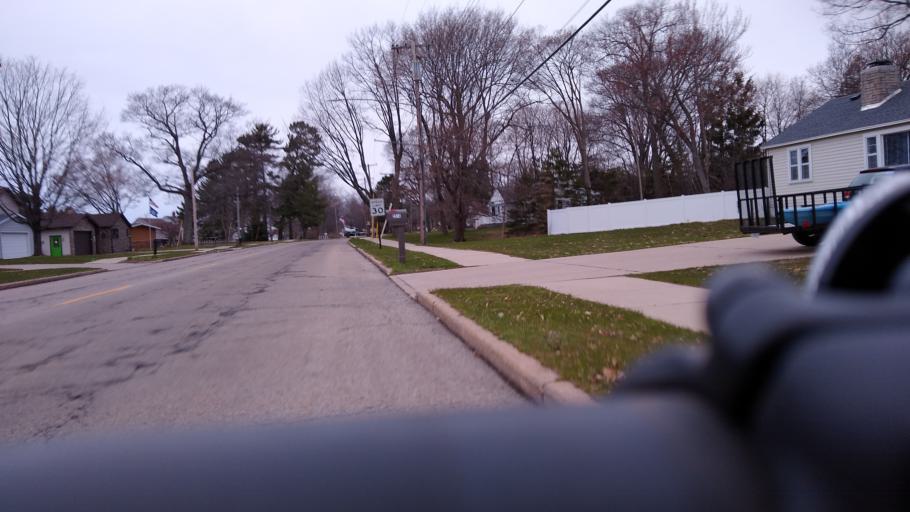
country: US
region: Michigan
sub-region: Delta County
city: Escanaba
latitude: 45.7184
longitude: -87.0733
